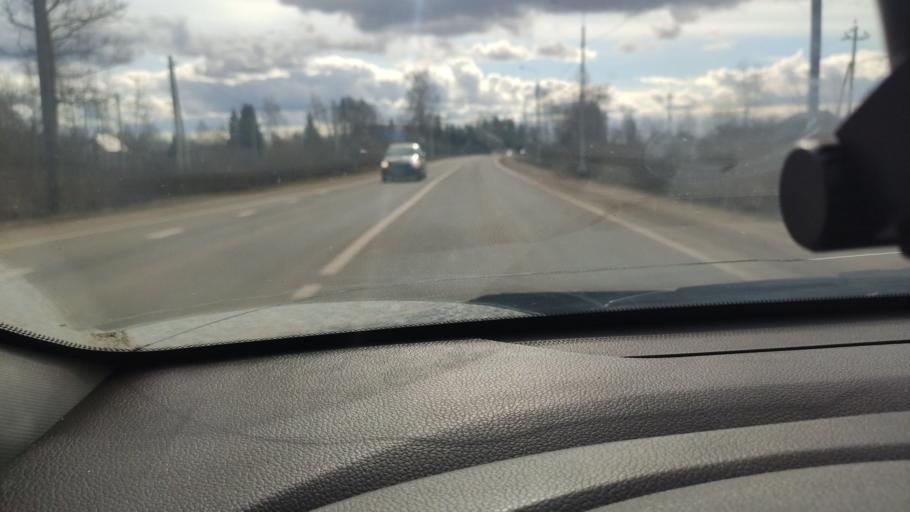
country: RU
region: Moskovskaya
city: Ruza
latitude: 55.7610
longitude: 36.1442
